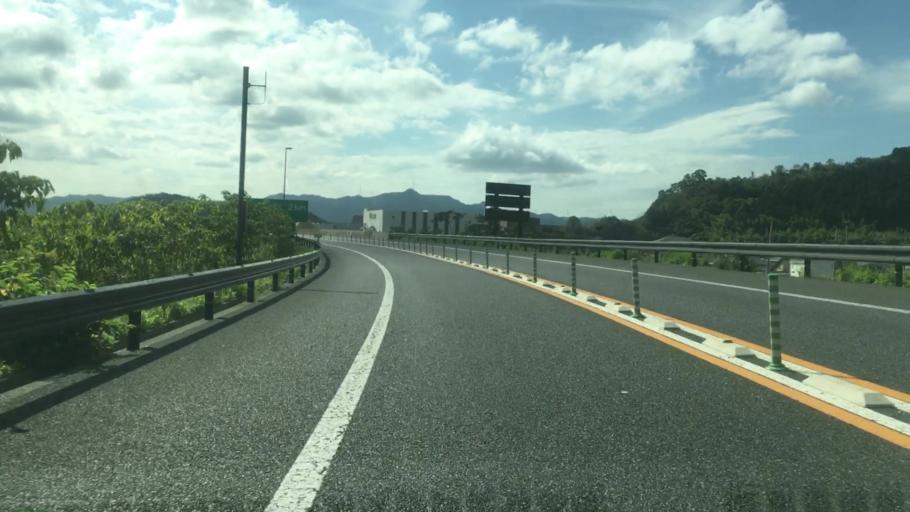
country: JP
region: Kyoto
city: Fukuchiyama
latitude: 35.1810
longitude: 135.0364
